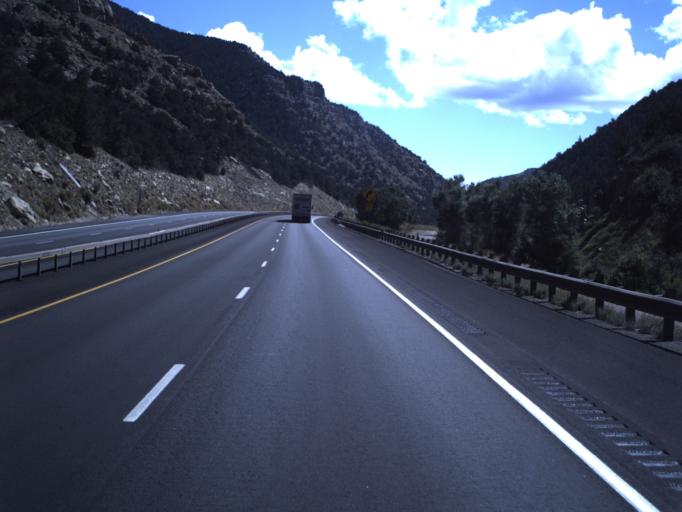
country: US
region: Utah
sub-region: Sevier County
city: Salina
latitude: 38.8954
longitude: -111.6267
